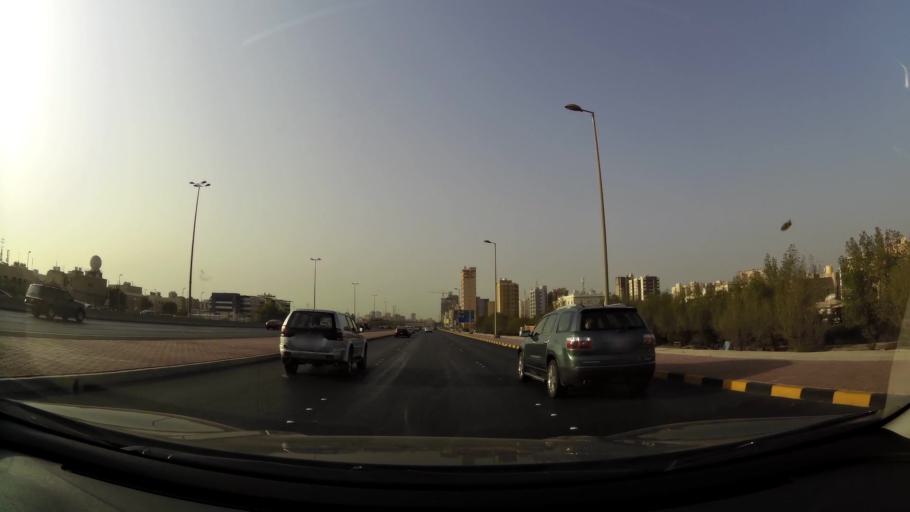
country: KW
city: Bayan
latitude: 29.3201
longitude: 48.0486
